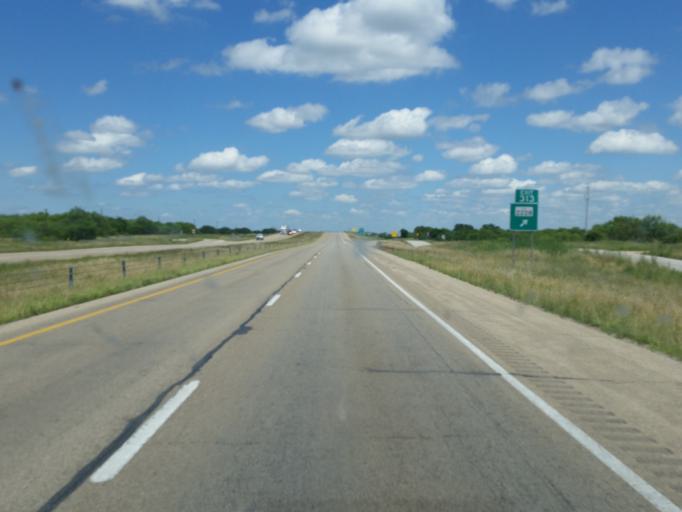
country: US
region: Texas
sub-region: Callahan County
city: Baird
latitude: 32.3865
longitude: -99.3041
